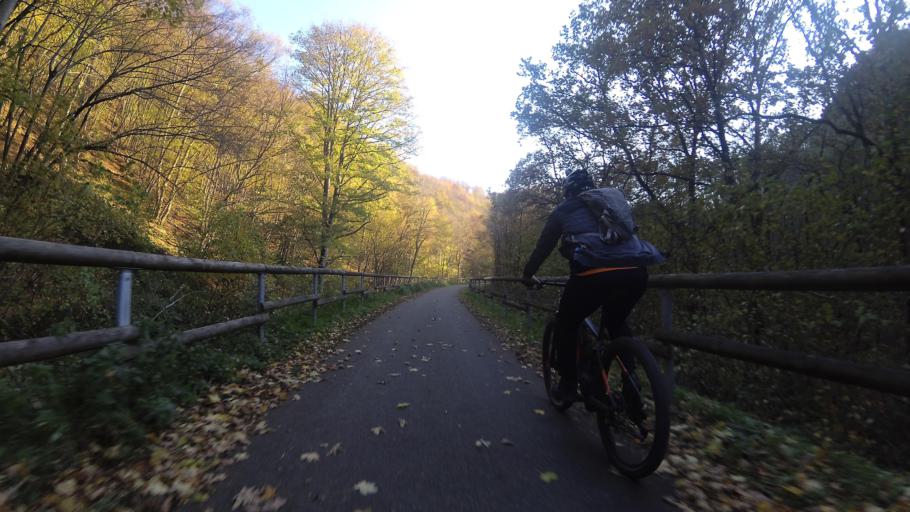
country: DE
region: Rheinland-Pfalz
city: Ollmuth
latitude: 49.6679
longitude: 6.7240
